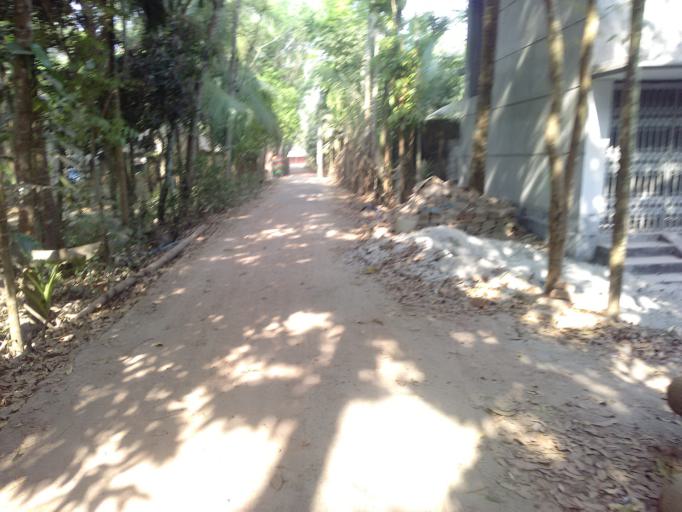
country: BD
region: Khulna
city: Khulna
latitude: 22.8971
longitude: 89.5292
